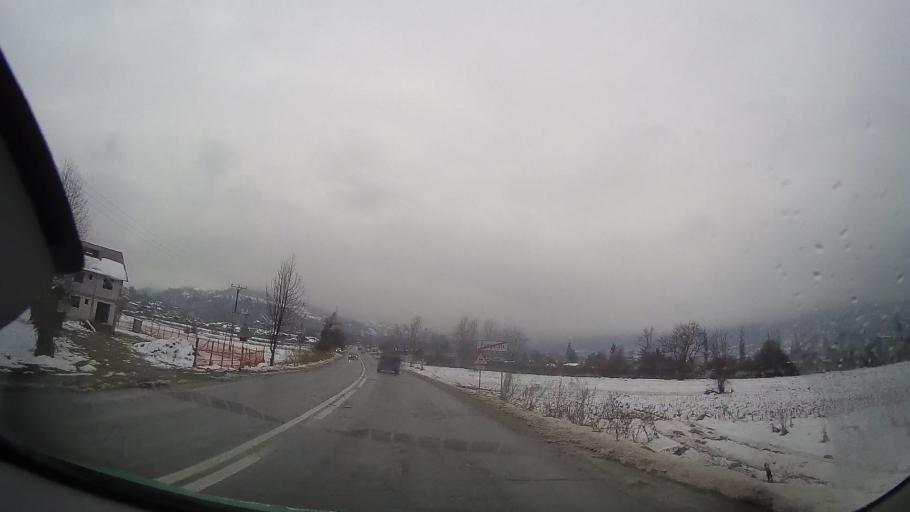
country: RO
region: Neamt
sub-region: Comuna Pangarati
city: Stejaru
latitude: 46.9226
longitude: 26.1896
